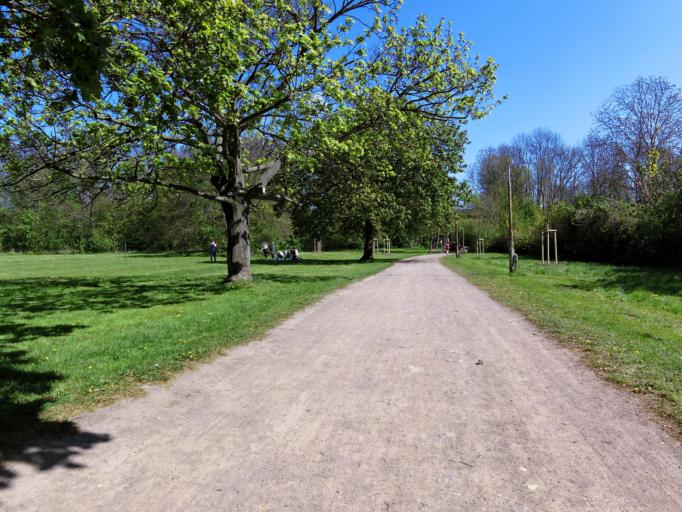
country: DE
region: Saxony
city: Leipzig
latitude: 51.3702
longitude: 12.3236
